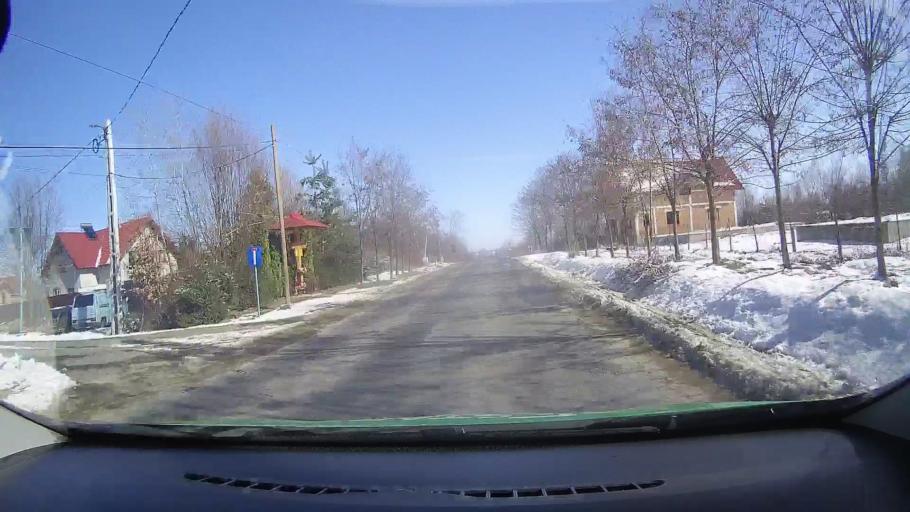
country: RO
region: Brasov
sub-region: Oras Victoria
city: Victoria
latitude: 45.7275
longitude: 24.7070
